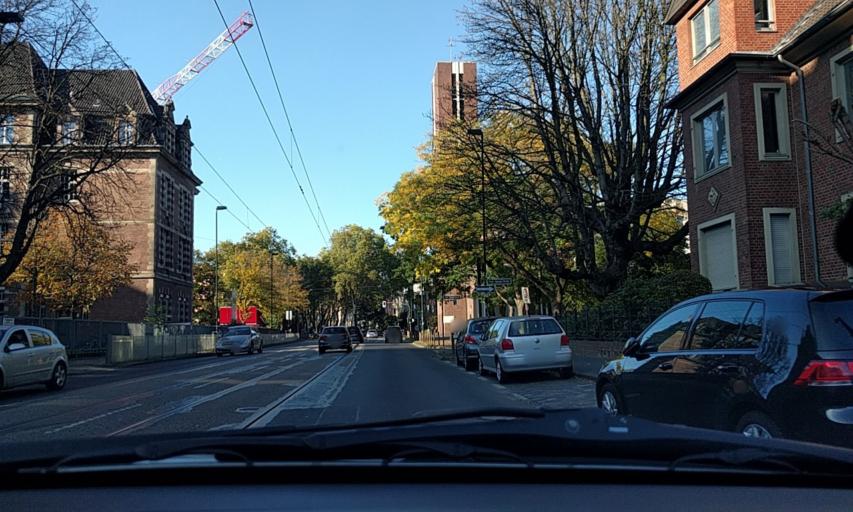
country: DE
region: North Rhine-Westphalia
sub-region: Regierungsbezirk Dusseldorf
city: Dusseldorf
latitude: 51.2342
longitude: 6.8076
